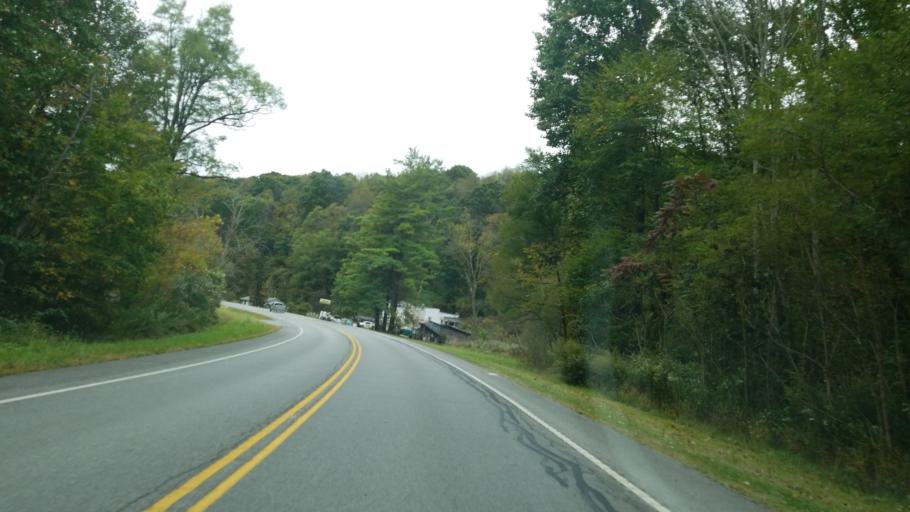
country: US
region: Pennsylvania
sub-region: Clearfield County
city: Curwensville
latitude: 40.9760
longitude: -78.5509
